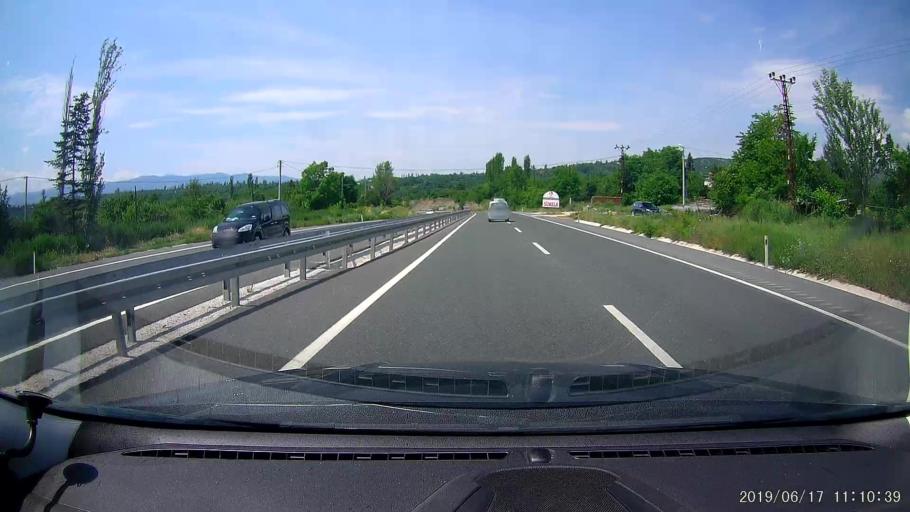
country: TR
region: Kastamonu
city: Tosya
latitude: 40.9972
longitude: 34.0205
